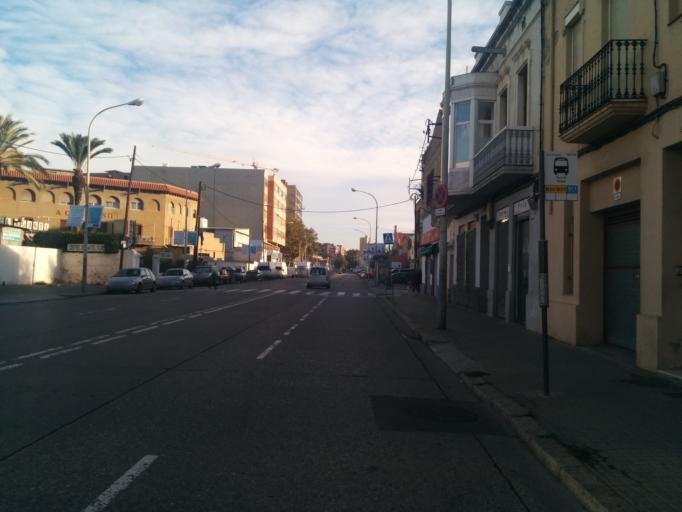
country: ES
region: Catalonia
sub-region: Provincia de Barcelona
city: Sant Marti
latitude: 41.4138
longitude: 2.2061
